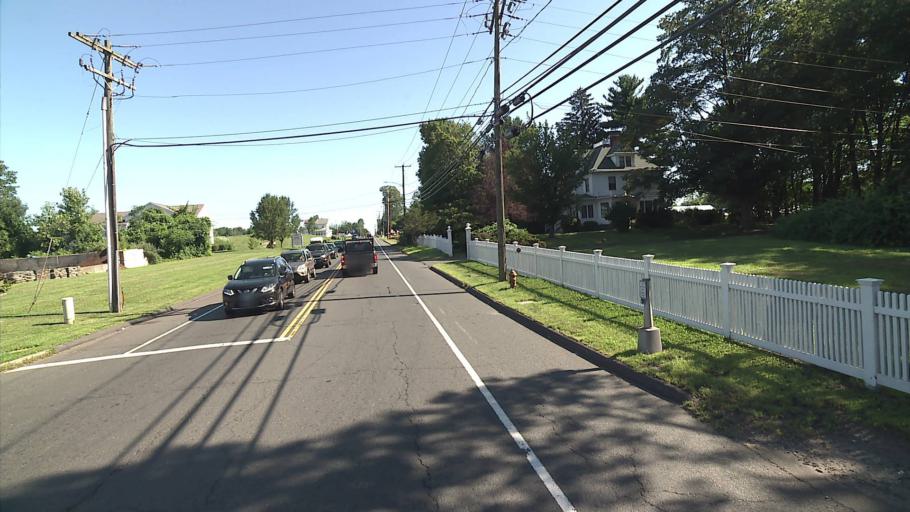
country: US
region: Connecticut
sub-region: New Haven County
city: Cheshire Village
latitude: 41.5355
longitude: -72.8940
